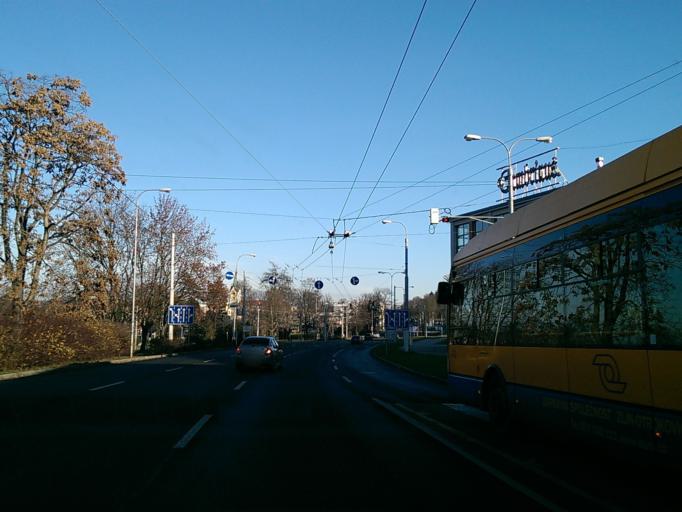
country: CZ
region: Zlin
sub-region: Okres Zlin
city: Zlin
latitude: 49.2233
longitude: 17.6612
